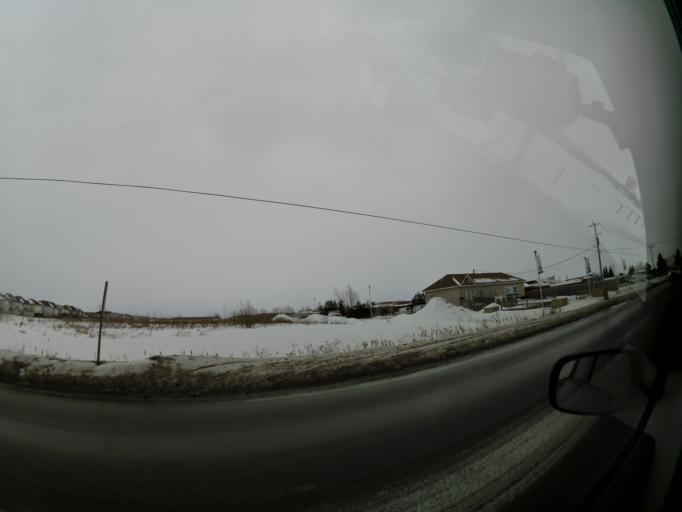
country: CA
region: Ontario
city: Clarence-Rockland
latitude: 45.4421
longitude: -75.4771
